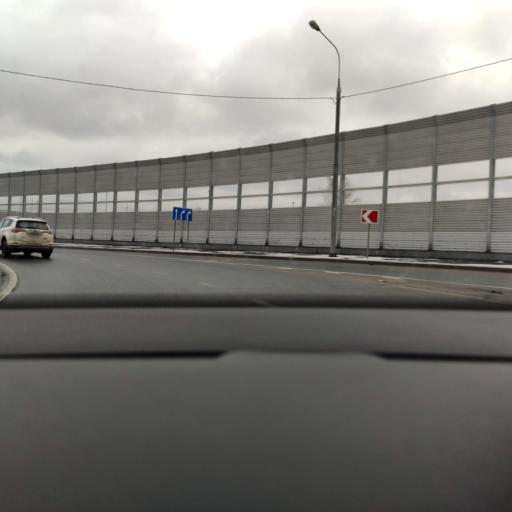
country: RU
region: Moskovskaya
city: Mamontovka
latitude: 55.9655
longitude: 37.8359
